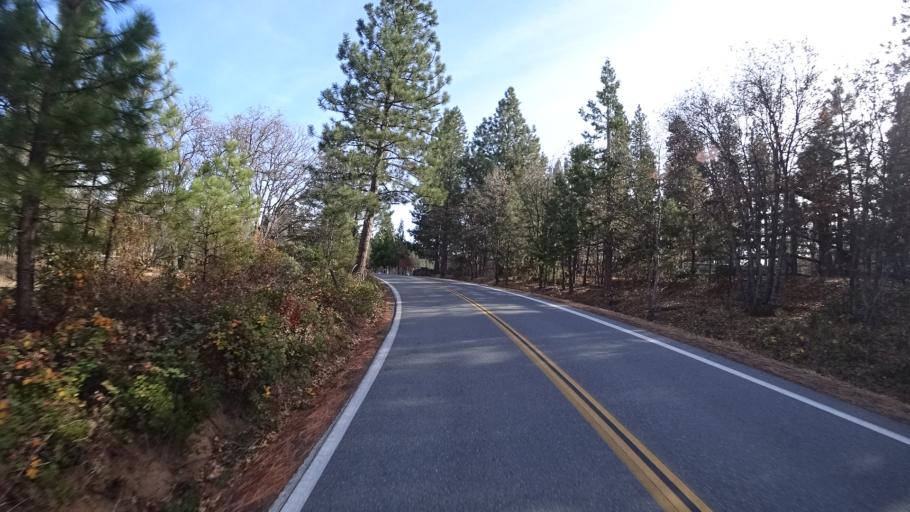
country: US
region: California
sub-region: Siskiyou County
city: Weed
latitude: 41.4024
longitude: -122.4252
